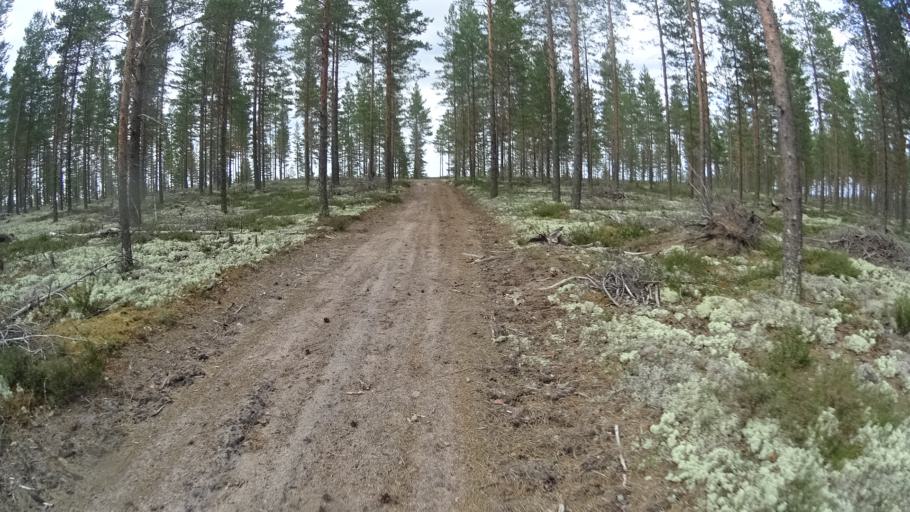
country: FI
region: Satakunta
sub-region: Pohjois-Satakunta
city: Jaemijaervi
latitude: 61.7710
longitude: 22.8043
